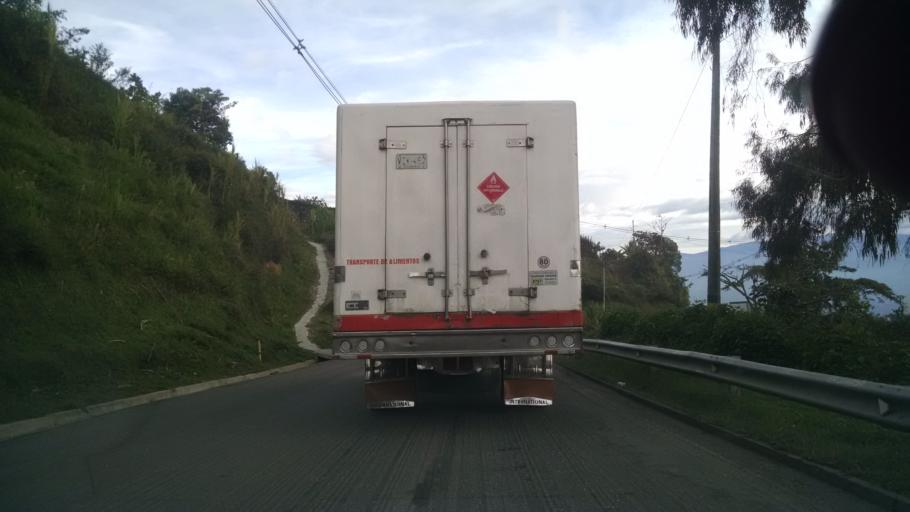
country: CO
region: Antioquia
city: Santa Barbara
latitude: 5.9074
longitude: -75.5748
